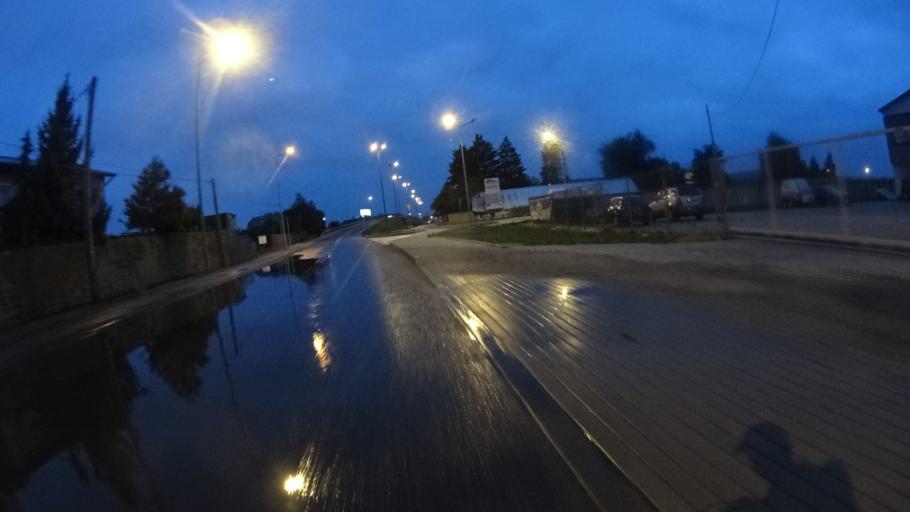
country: PL
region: Masovian Voivodeship
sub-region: Warszawa
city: Ursus
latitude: 52.2281
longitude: 20.8803
